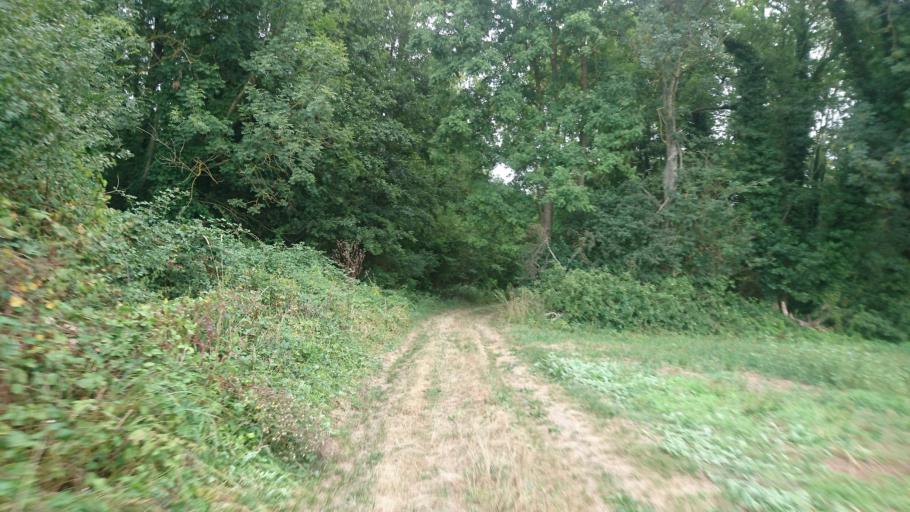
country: FR
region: Bourgogne
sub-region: Departement de l'Yonne
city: Fleury-la-Vallee
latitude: 47.8654
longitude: 3.3996
